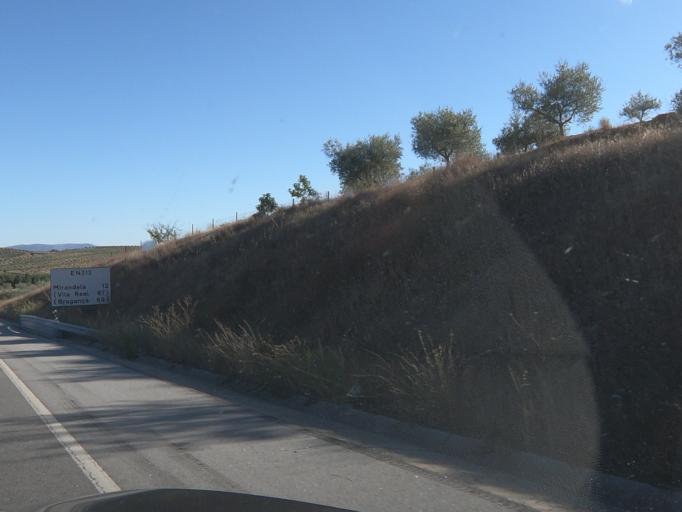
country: PT
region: Vila Real
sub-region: Valpacos
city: Valpacos
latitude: 41.5625
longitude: -7.2678
